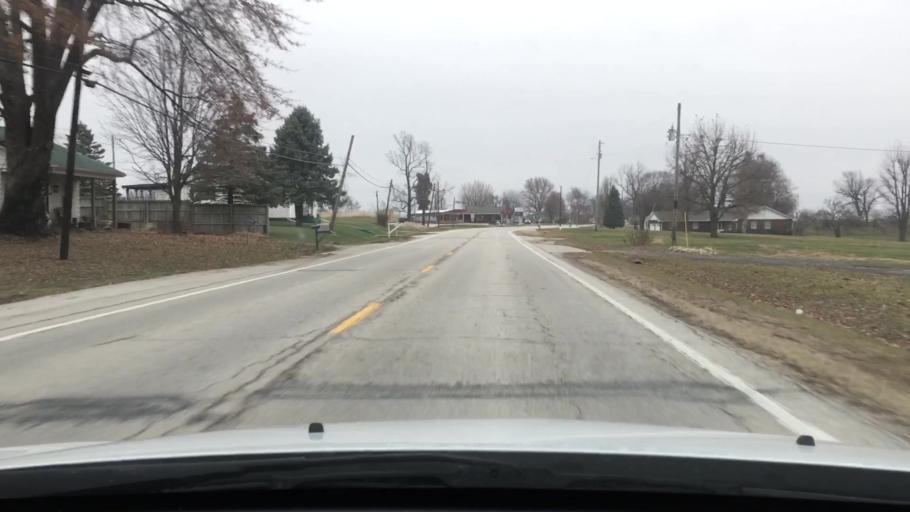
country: US
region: Illinois
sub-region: Pike County
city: Pittsfield
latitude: 39.5743
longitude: -90.9115
